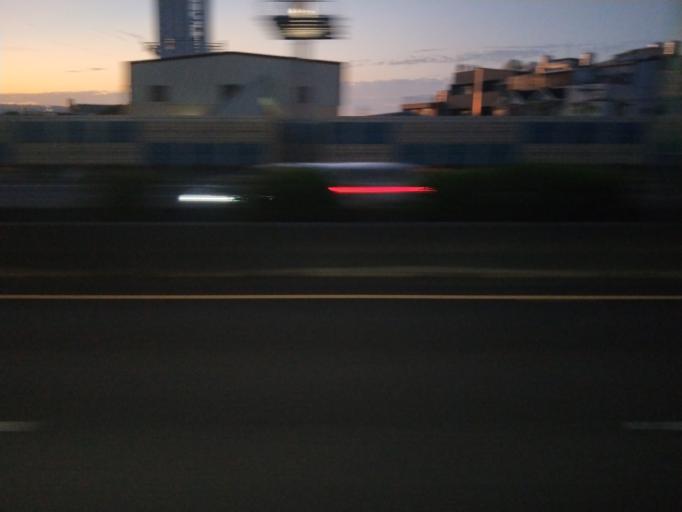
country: TW
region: Taiwan
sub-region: Taichung City
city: Taichung
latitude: 24.1986
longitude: 120.6455
